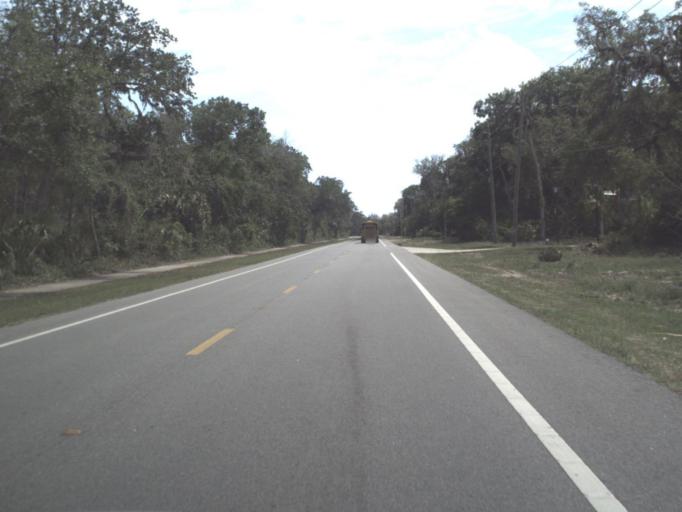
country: US
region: Florida
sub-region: Flagler County
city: Palm Coast
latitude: 29.5713
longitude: -81.1843
